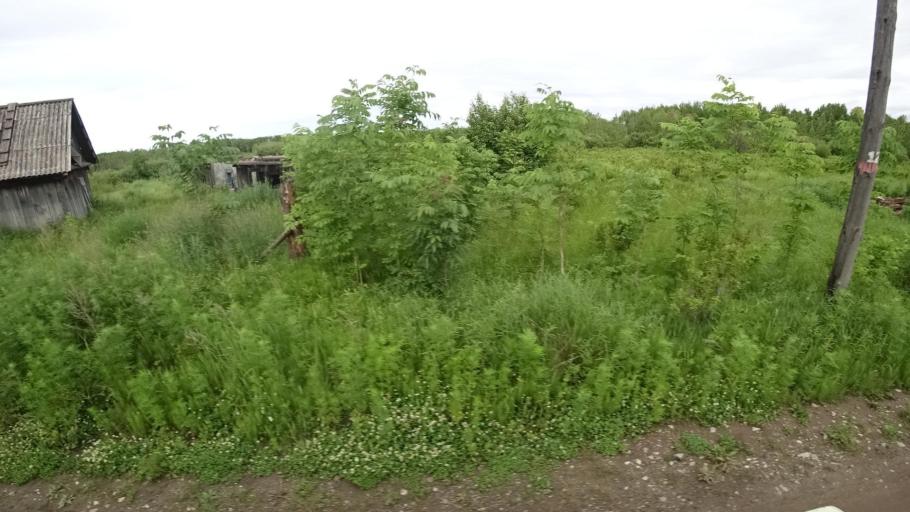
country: RU
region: Khabarovsk Krai
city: Amursk
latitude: 49.8831
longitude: 136.1276
